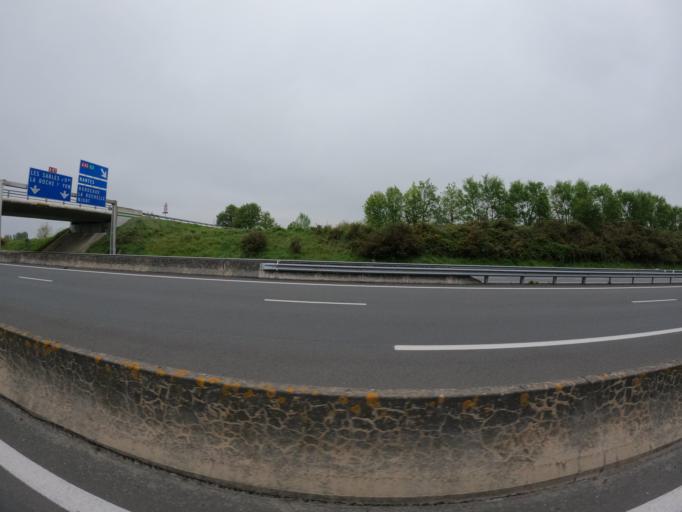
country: FR
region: Pays de la Loire
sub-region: Departement de la Vendee
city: Les Essarts
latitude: 46.8111
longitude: -1.2007
